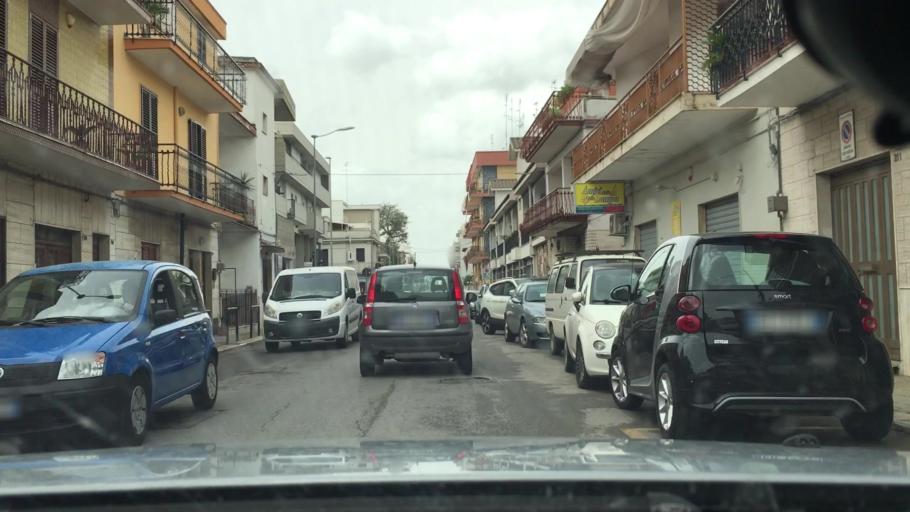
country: IT
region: Apulia
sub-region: Provincia di Bari
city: Capurso
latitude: 41.0477
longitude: 16.9262
